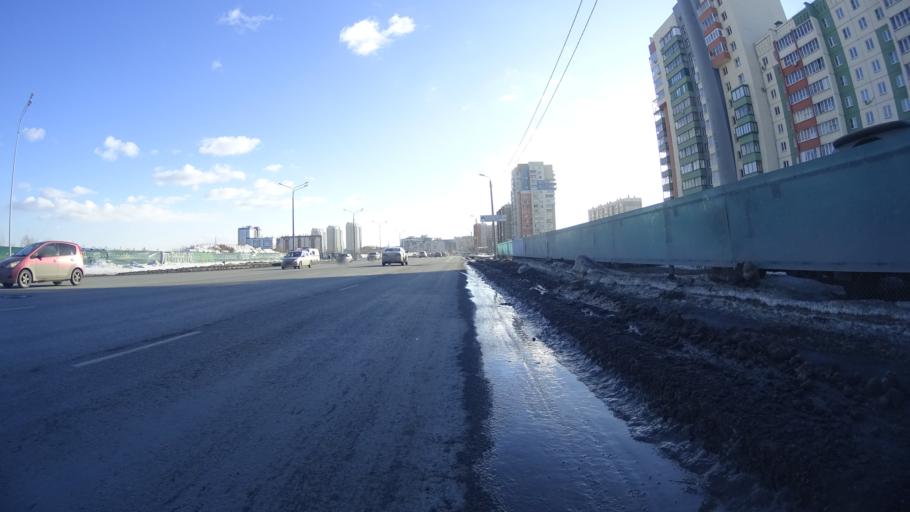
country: RU
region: Chelyabinsk
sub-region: Gorod Chelyabinsk
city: Chelyabinsk
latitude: 55.1649
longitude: 61.3024
